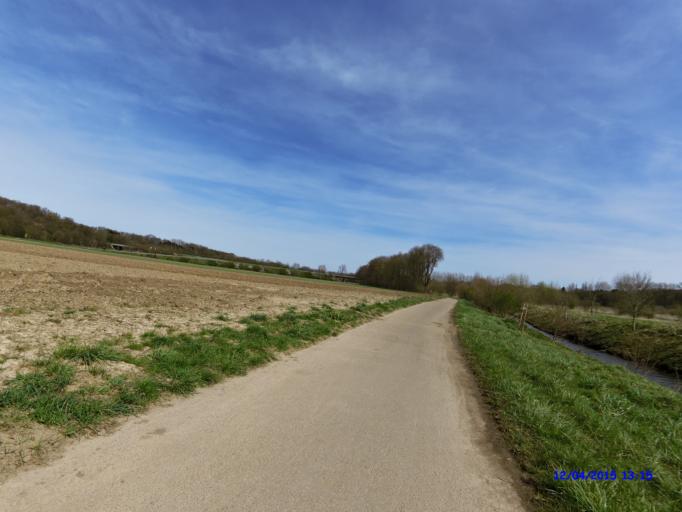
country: DE
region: North Rhine-Westphalia
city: Geilenkirchen
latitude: 50.9509
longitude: 6.1054
